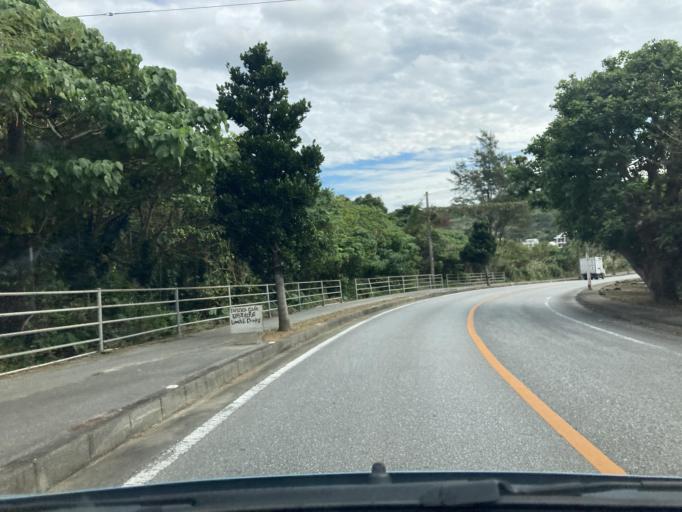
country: JP
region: Okinawa
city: Ishikawa
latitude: 26.4373
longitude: 127.7799
